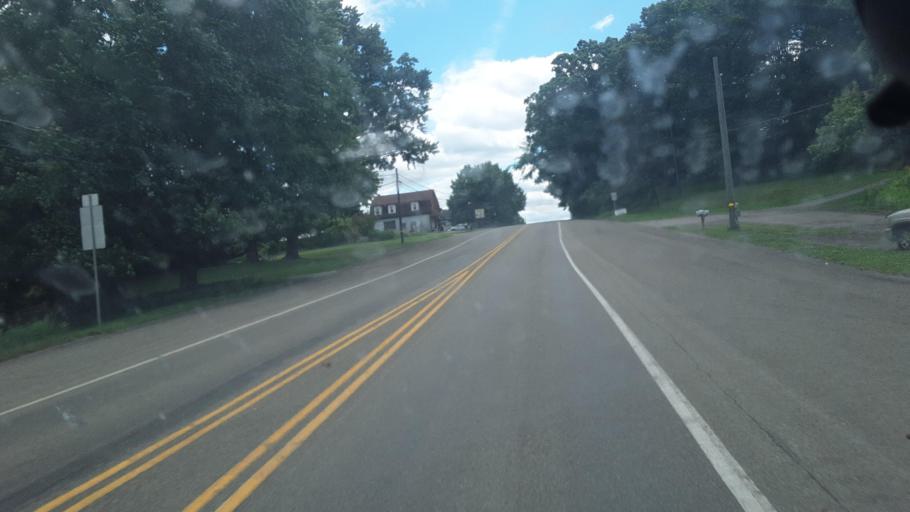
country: US
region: Pennsylvania
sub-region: Butler County
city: Prospect
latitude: 40.9650
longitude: -80.1603
